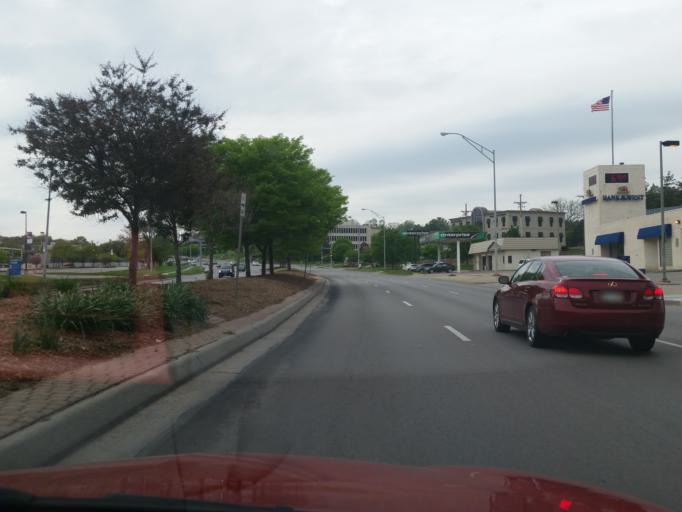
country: US
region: Nebraska
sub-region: Douglas County
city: Ralston
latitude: 41.2624
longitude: -96.0443
